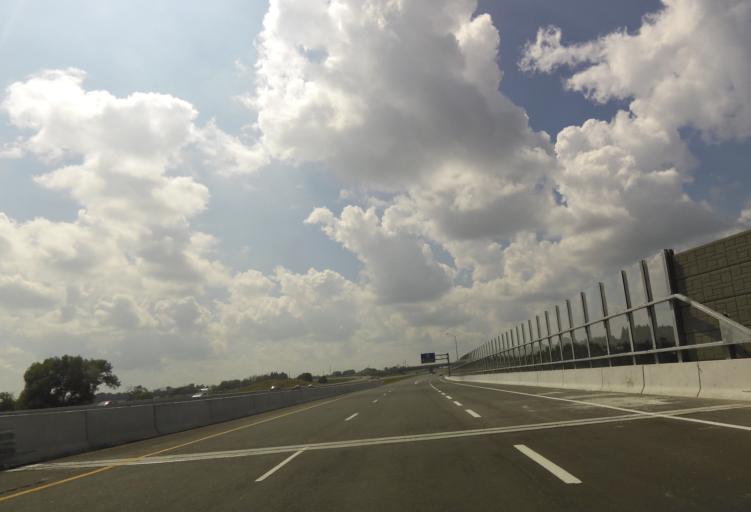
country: CA
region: Ontario
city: Oshawa
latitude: 43.9487
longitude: -78.9519
